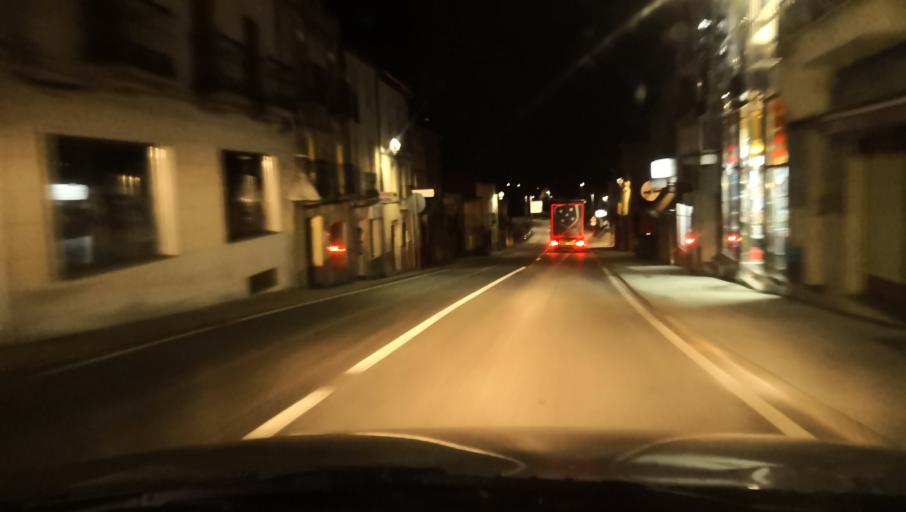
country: ES
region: Castille and Leon
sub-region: Provincia de Zamora
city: Alcanices
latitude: 41.6991
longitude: -6.3481
